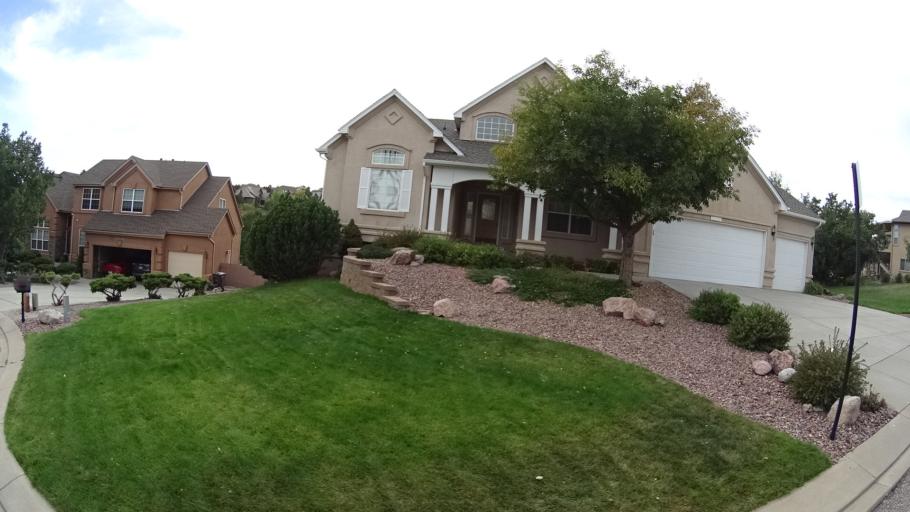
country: US
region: Colorado
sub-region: El Paso County
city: Colorado Springs
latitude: 38.9025
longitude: -104.7855
